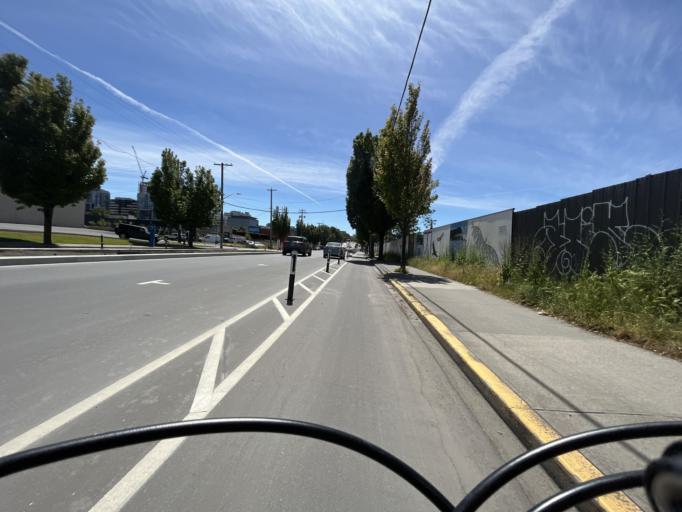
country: CA
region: British Columbia
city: Victoria
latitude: 48.4340
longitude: -123.3674
